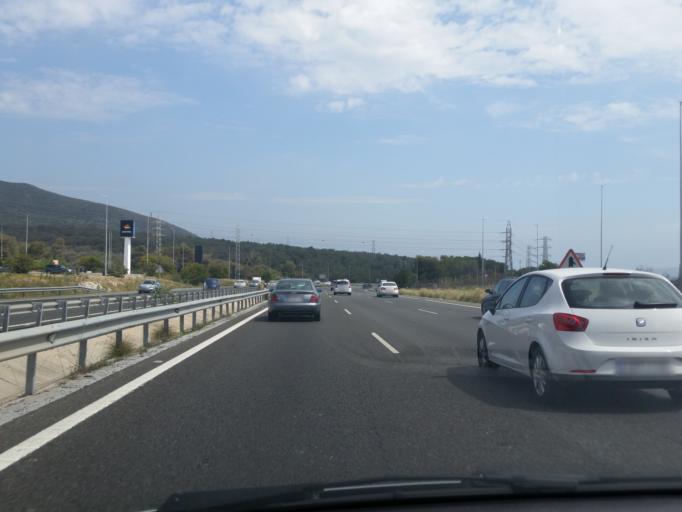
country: ES
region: Andalusia
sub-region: Provincia de Malaga
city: Torremolinos
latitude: 36.6122
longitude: -4.5284
